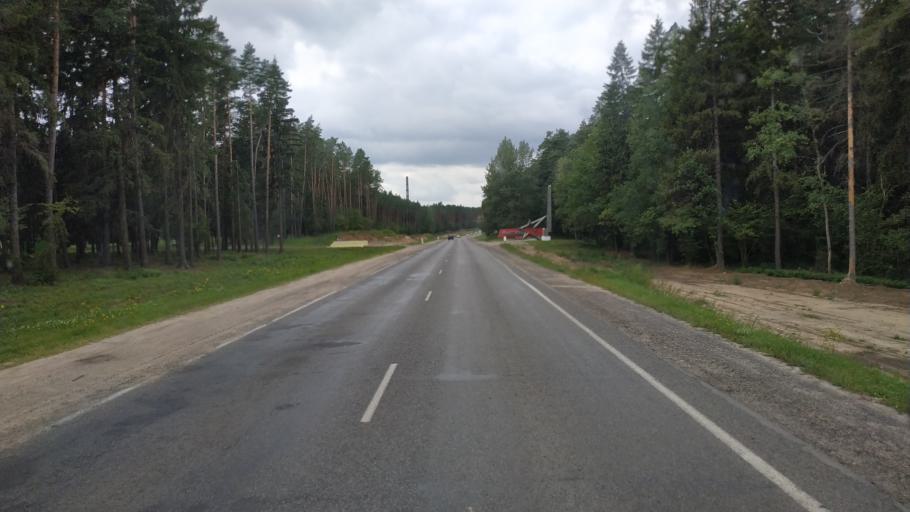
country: BY
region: Mogilev
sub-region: Mahilyowski Rayon
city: Veyno
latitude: 53.8766
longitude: 30.4235
